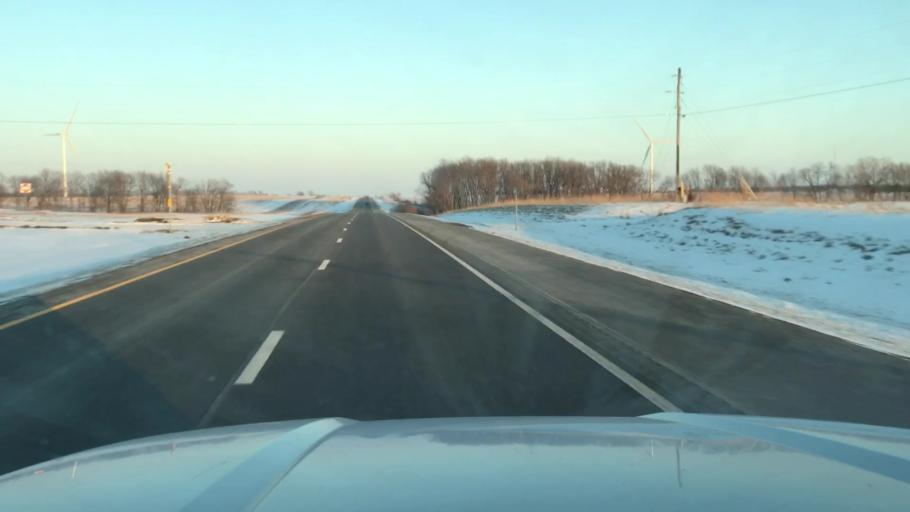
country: US
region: Missouri
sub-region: DeKalb County
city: Maysville
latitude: 39.7617
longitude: -94.3886
